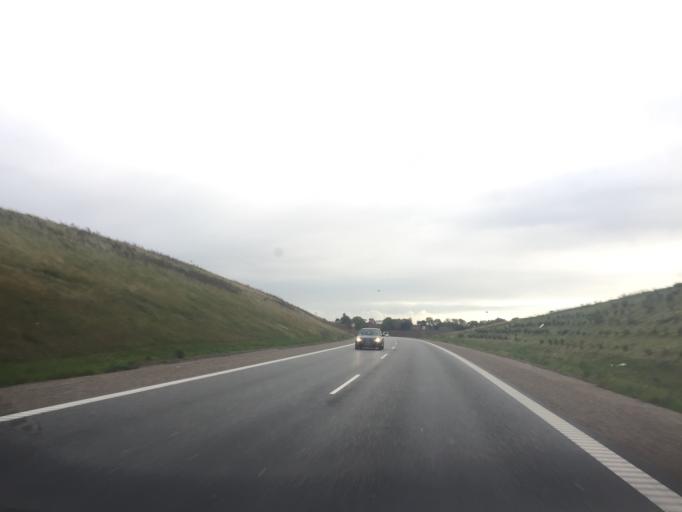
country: DK
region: Capital Region
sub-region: Egedal Kommune
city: Smorumnedre
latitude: 55.7452
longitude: 12.2821
